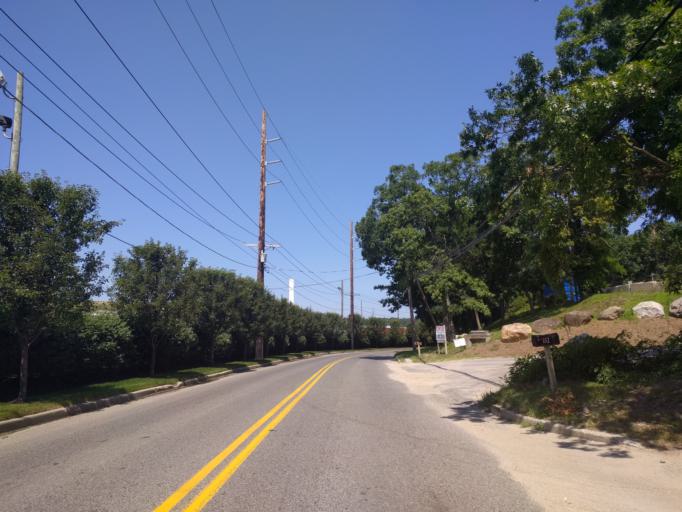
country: US
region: New York
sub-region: Suffolk County
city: Kings Park
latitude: 40.8769
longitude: -73.2822
